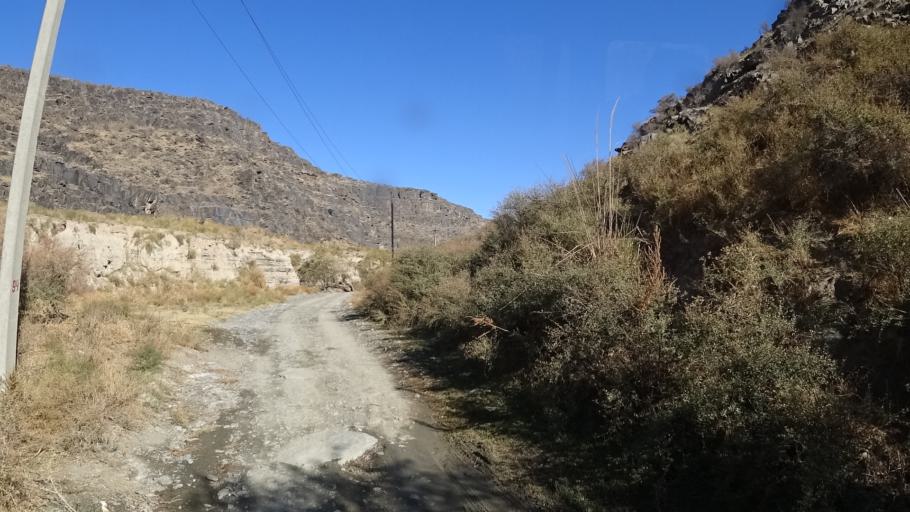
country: UZ
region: Navoiy
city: Nurota
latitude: 40.3081
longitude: 65.6199
